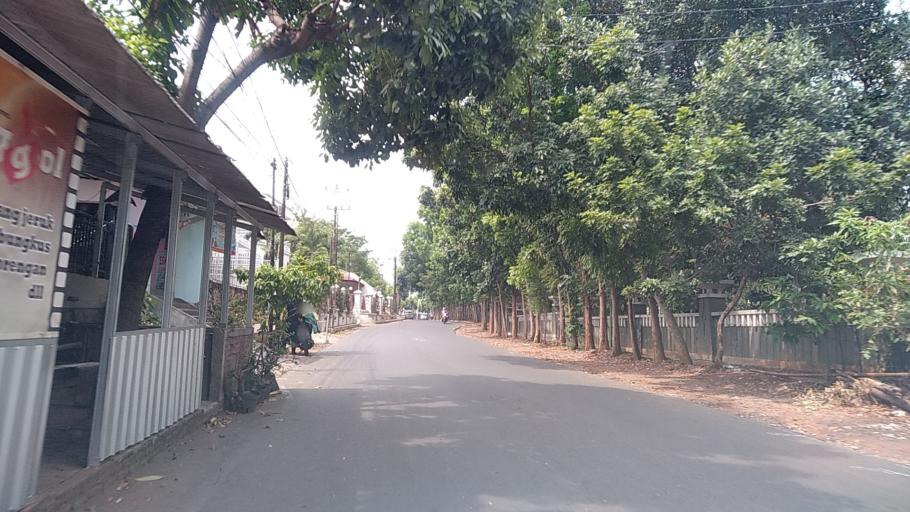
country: ID
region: Central Java
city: Semarang
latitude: -7.0532
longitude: 110.4323
